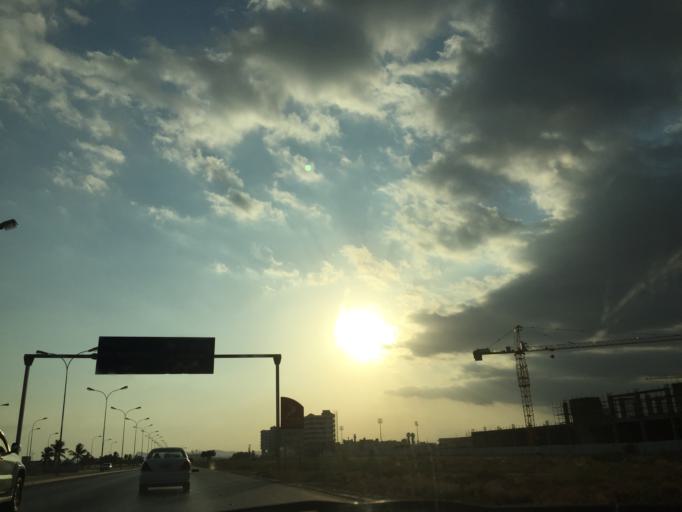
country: OM
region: Zufar
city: Salalah
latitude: 16.9982
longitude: 54.0336
